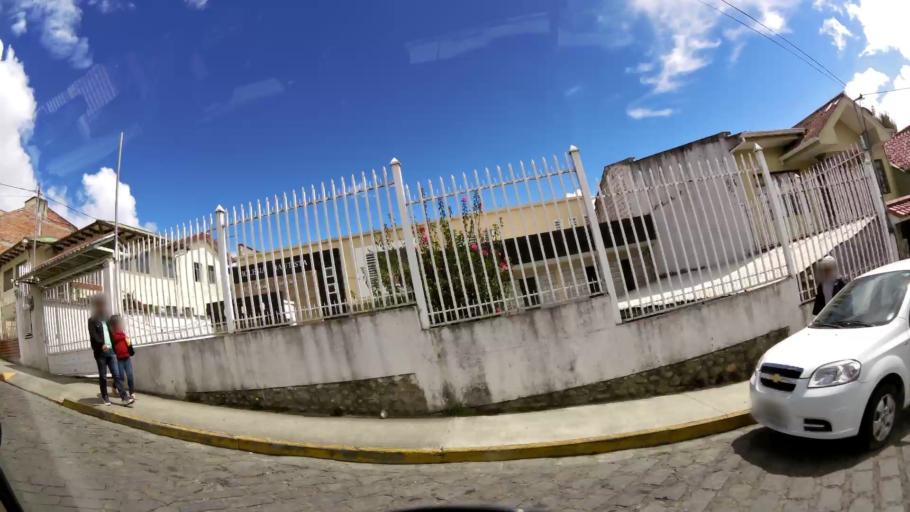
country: EC
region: Canar
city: Azogues
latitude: -2.7364
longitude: -78.8435
